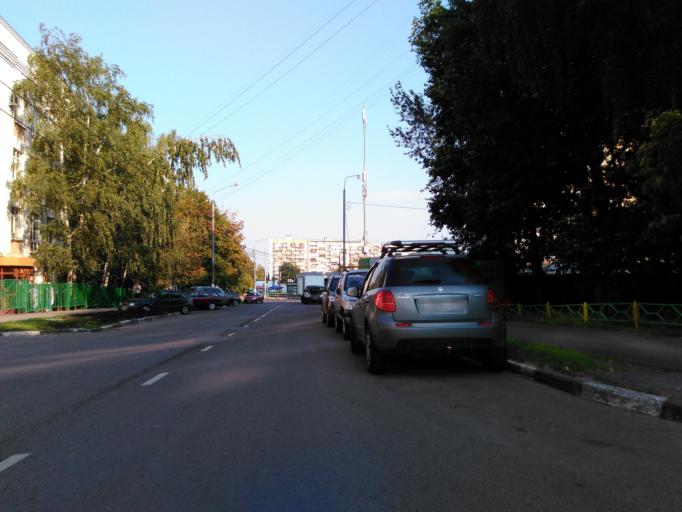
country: RU
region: Moskovskaya
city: Cheremushki
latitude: 55.6433
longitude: 37.5396
